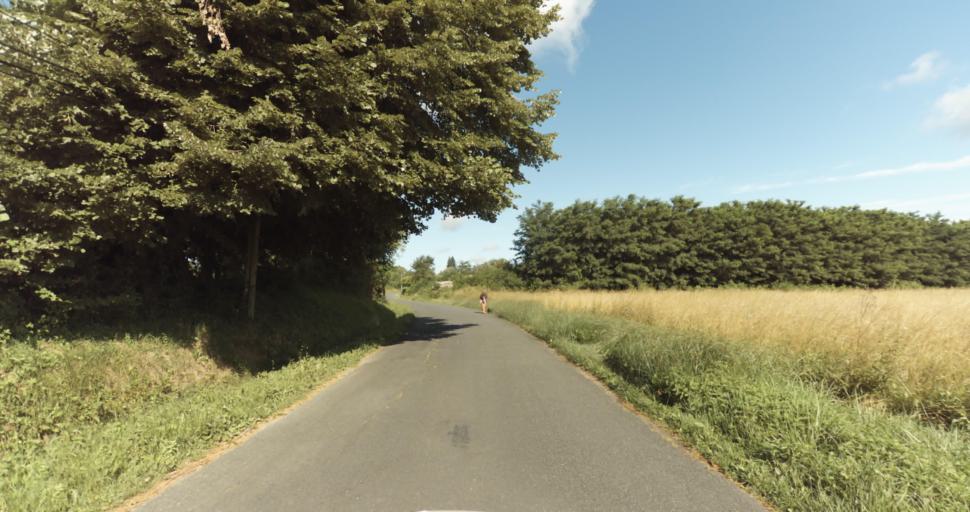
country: FR
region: Aquitaine
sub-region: Departement de la Gironde
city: Bazas
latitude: 44.4255
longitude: -0.2091
